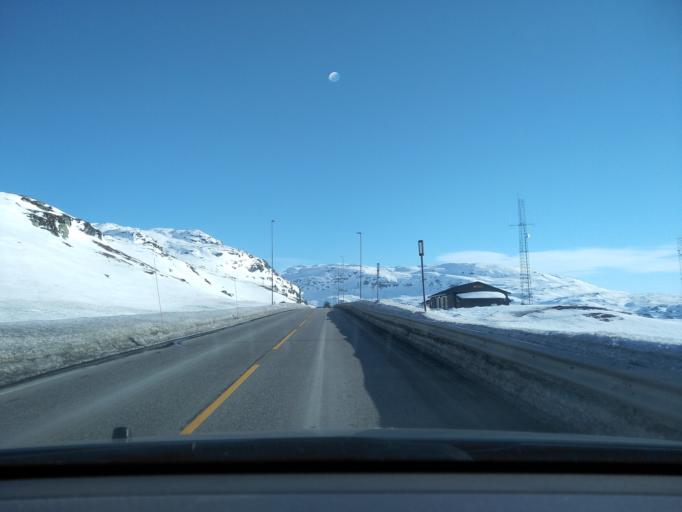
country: NO
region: Aust-Agder
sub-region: Bykle
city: Hovden
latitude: 59.8410
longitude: 6.9819
